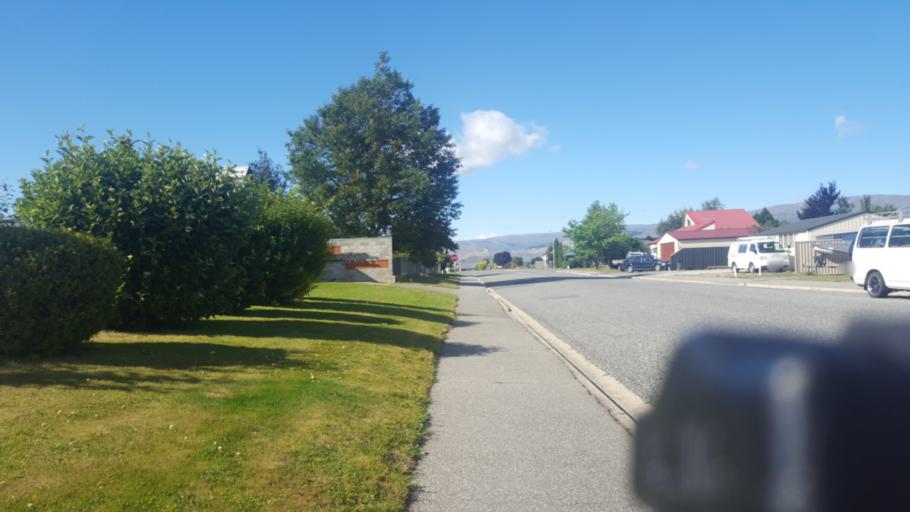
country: NZ
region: Otago
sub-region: Queenstown-Lakes District
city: Wanaka
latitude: -45.0458
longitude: 169.2001
